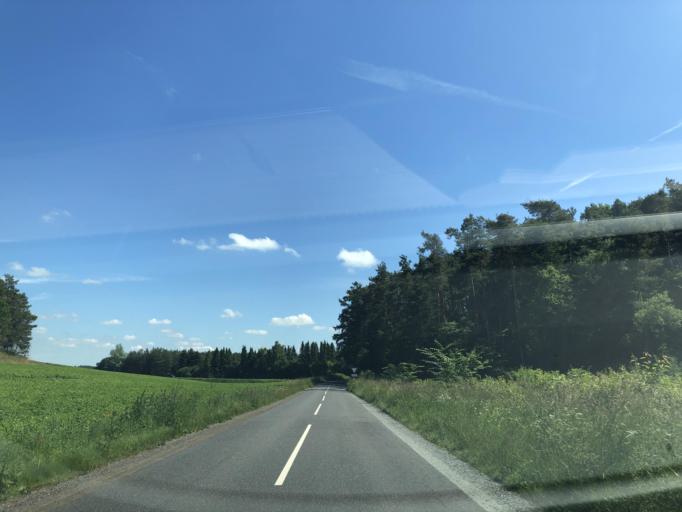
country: DK
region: North Denmark
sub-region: Mariagerfjord Kommune
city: Hobro
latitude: 56.6161
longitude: 9.6995
